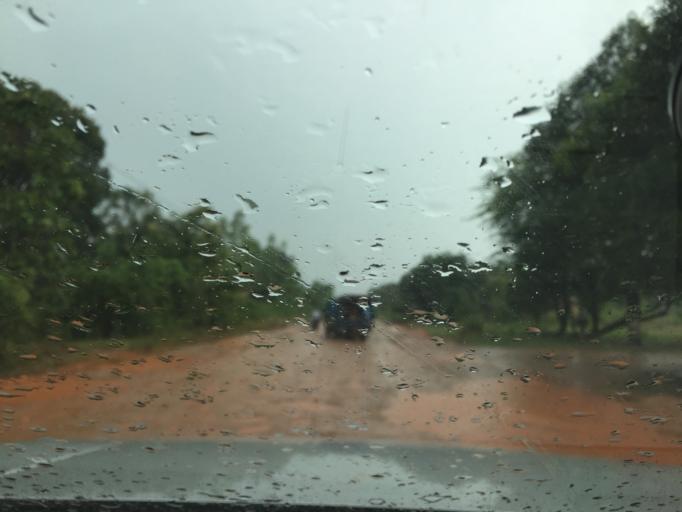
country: LA
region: Attapu
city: Attapu
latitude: 14.8287
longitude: 106.8013
